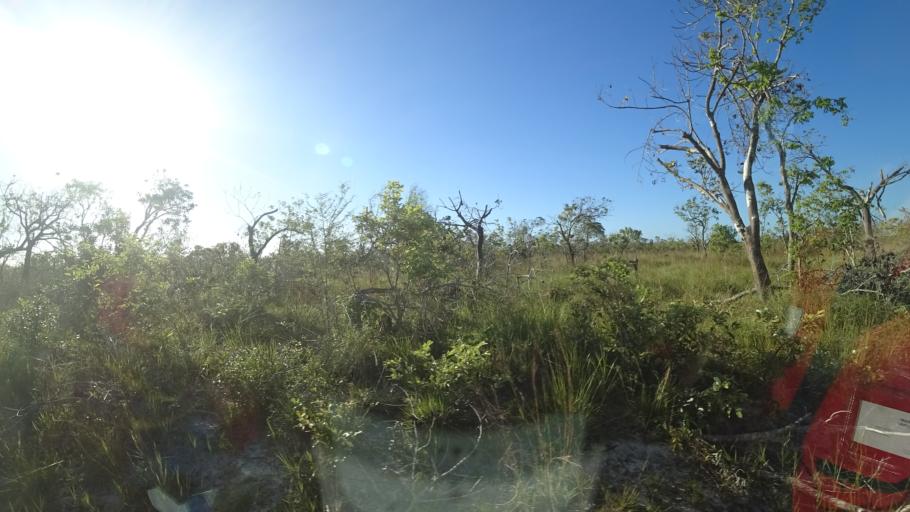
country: MZ
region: Sofala
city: Beira
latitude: -19.5722
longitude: 35.2331
